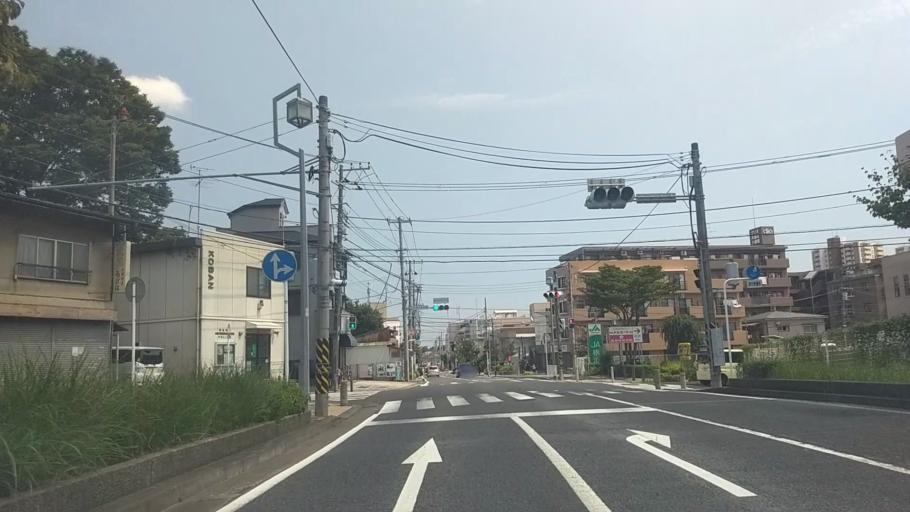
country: JP
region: Kanagawa
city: Yokohama
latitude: 35.4881
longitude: 139.6093
